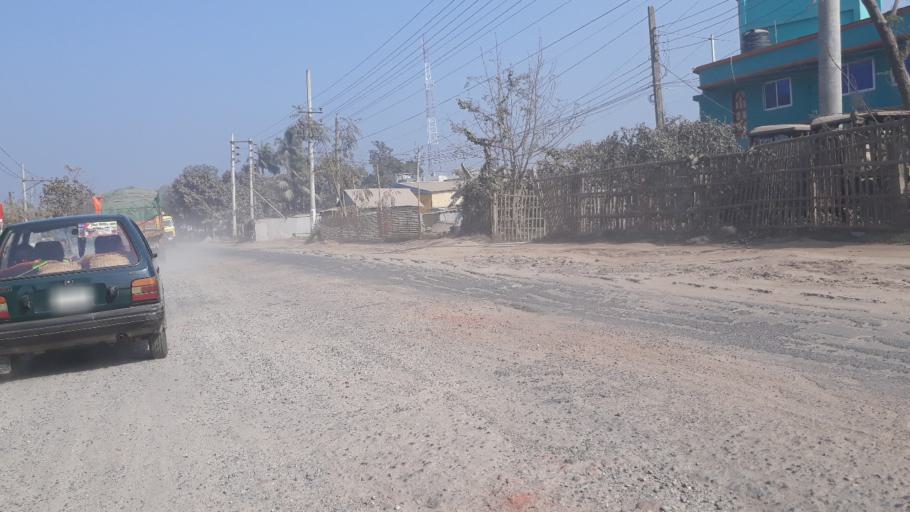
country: BD
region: Khulna
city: Kushtia
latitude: 23.8864
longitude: 89.1062
